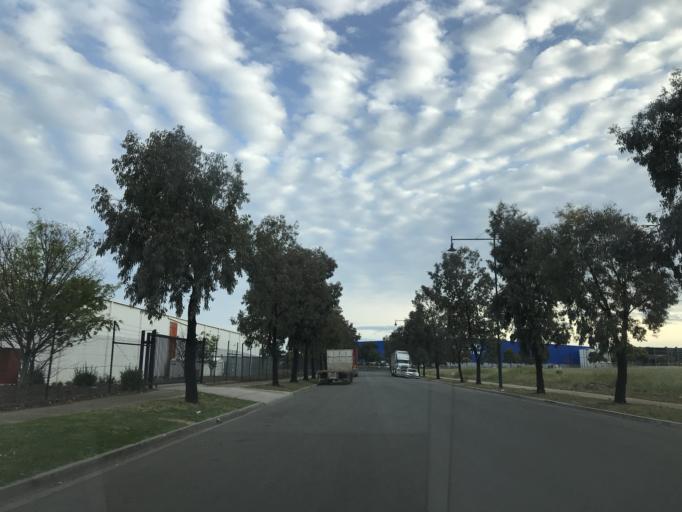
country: AU
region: Victoria
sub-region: Wyndham
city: Truganina
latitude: -37.8013
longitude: 144.7558
